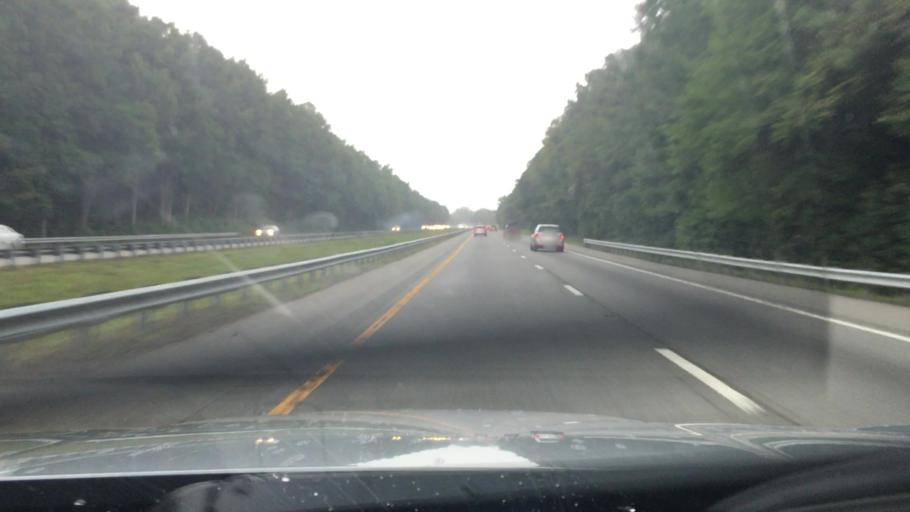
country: US
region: North Carolina
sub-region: Halifax County
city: Halifax
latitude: 36.3150
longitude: -77.7063
